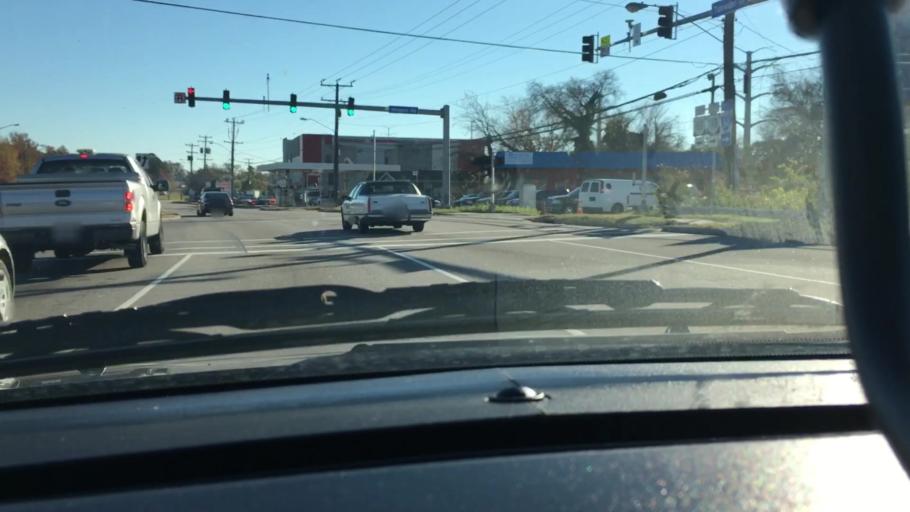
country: US
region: Virginia
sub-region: City of Norfolk
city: Norfolk
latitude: 36.9018
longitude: -76.2566
